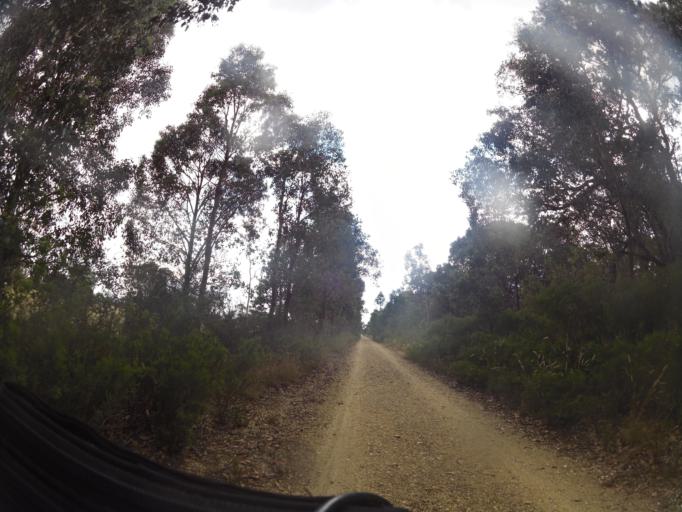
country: AU
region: Victoria
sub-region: Wellington
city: Heyfield
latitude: -38.0341
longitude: 146.6569
